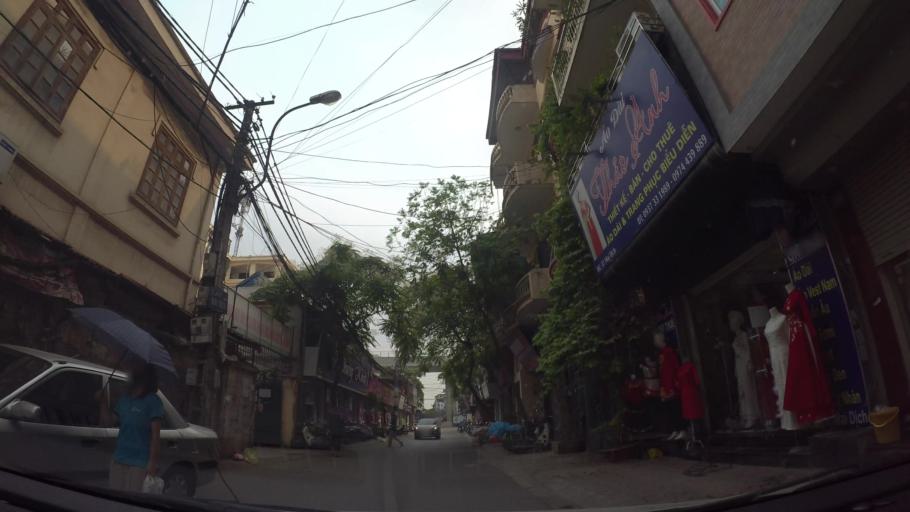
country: VN
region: Ha Noi
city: Cau Dien
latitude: 21.0386
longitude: 105.7739
